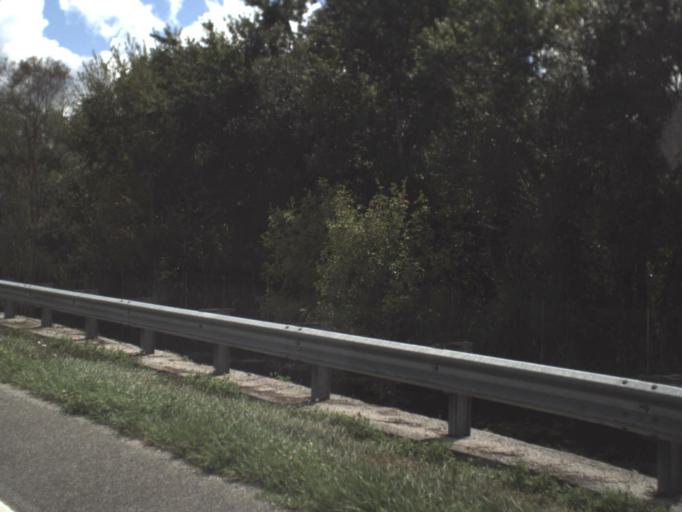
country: US
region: Florida
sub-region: DeSoto County
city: Arcadia
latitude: 27.2606
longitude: -81.9806
